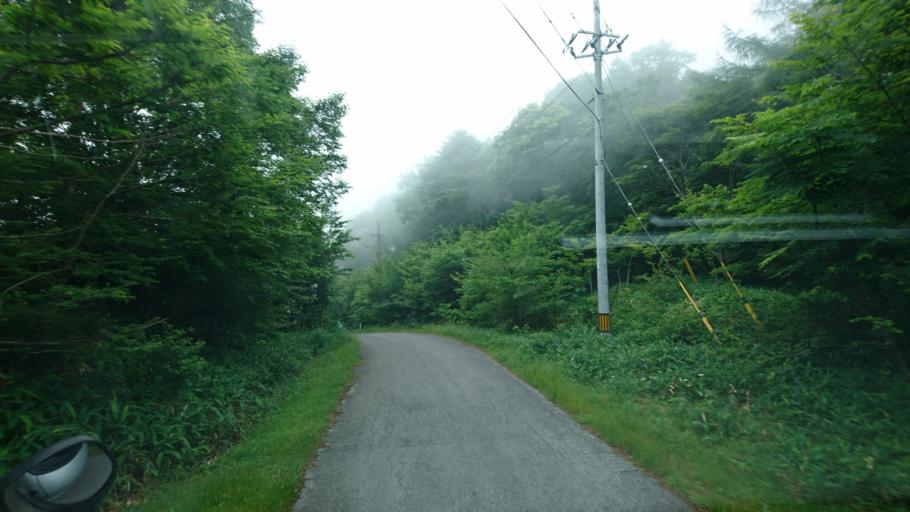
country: JP
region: Iwate
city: Ofunato
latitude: 39.1561
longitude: 141.7513
